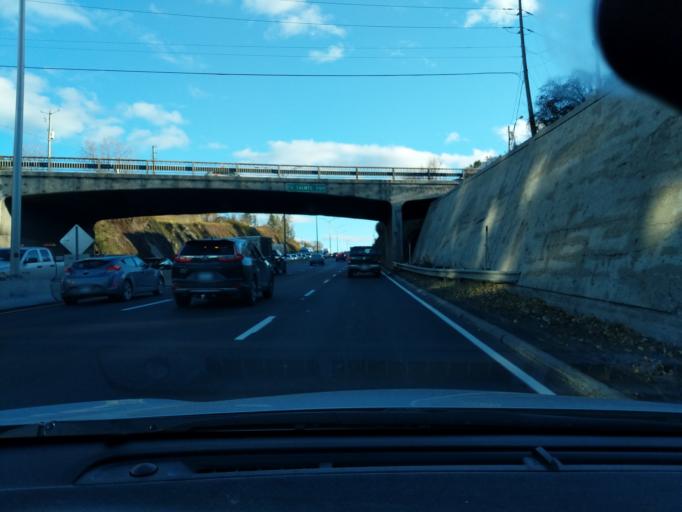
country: CA
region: Quebec
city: L'Ancienne-Lorette
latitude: 46.7779
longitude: -71.3072
